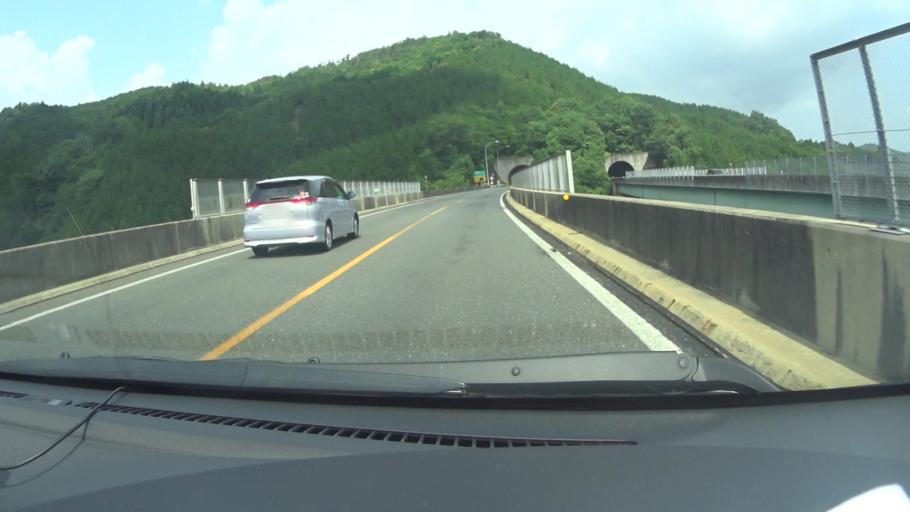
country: JP
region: Kyoto
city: Kameoka
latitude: 34.9927
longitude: 135.5790
